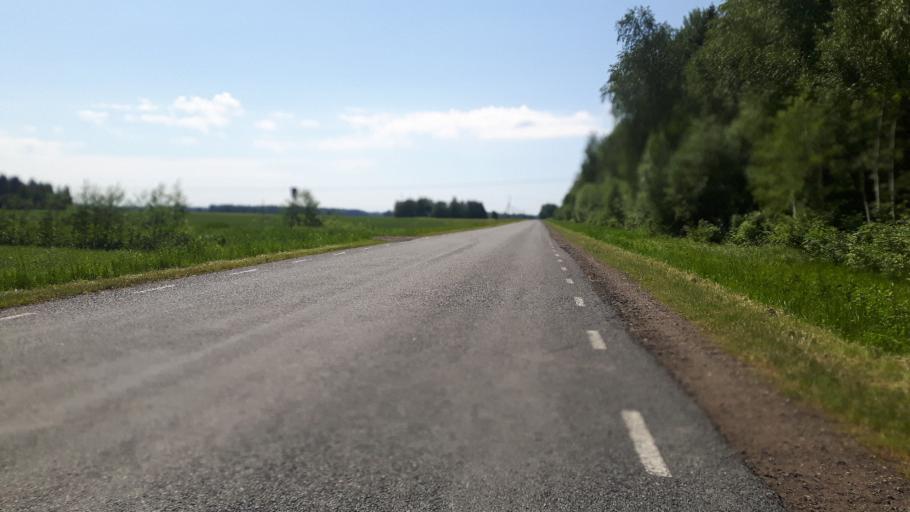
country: EE
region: Paernumaa
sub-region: Vaendra vald (alev)
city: Vandra
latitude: 58.6293
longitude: 25.0209
